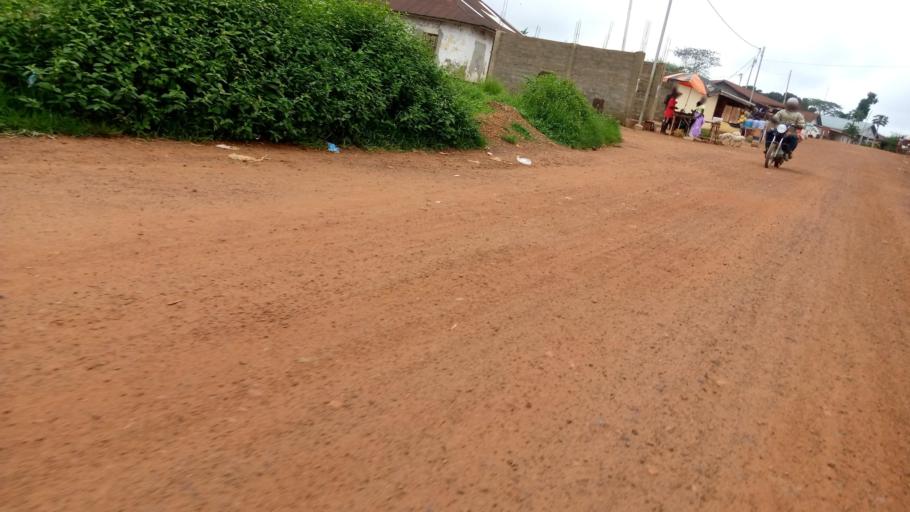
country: SL
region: Southern Province
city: Gandorhun
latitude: 7.4340
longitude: -11.8409
